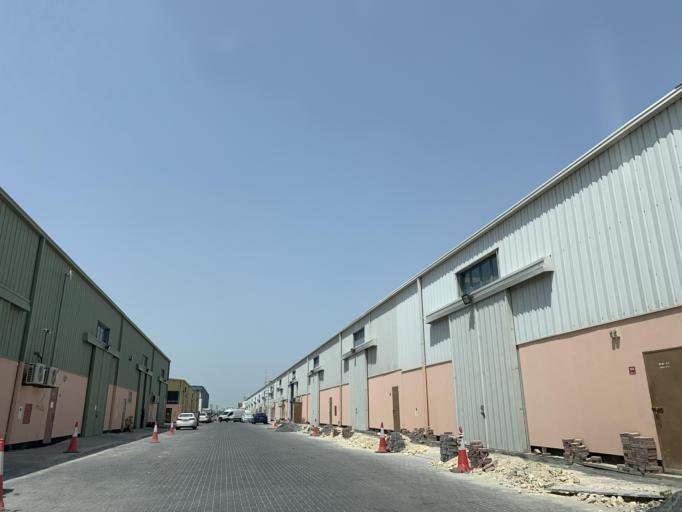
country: BH
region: Northern
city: Madinat `Isa
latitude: 26.1901
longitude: 50.5413
